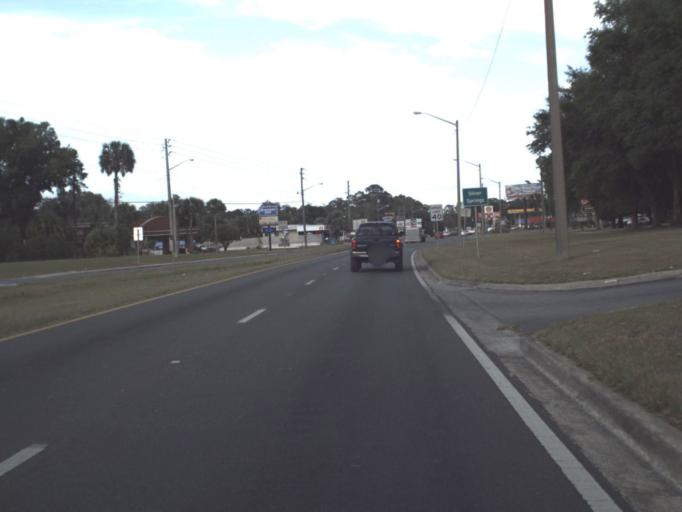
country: US
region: Florida
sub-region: Marion County
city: Ocala
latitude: 29.2109
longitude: -82.0655
